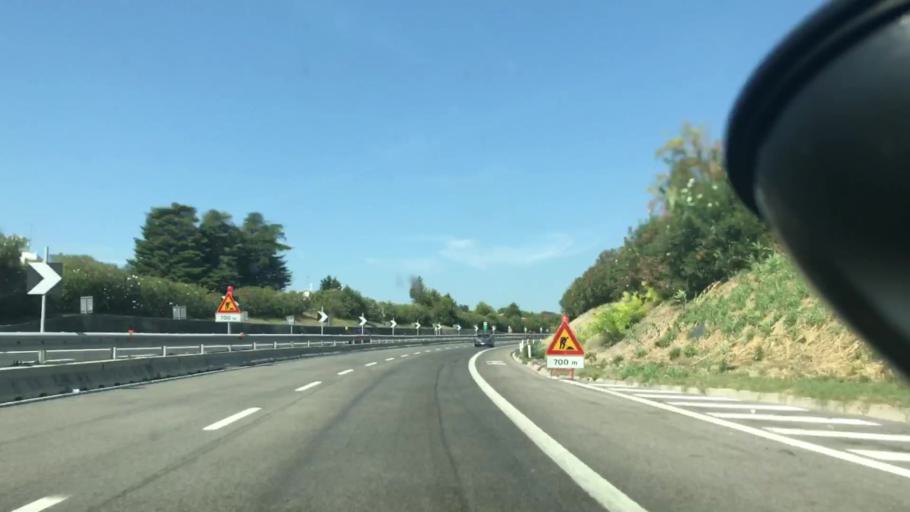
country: IT
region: Abruzzo
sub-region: Provincia di Chieti
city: San Salvo
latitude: 42.0643
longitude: 14.7301
